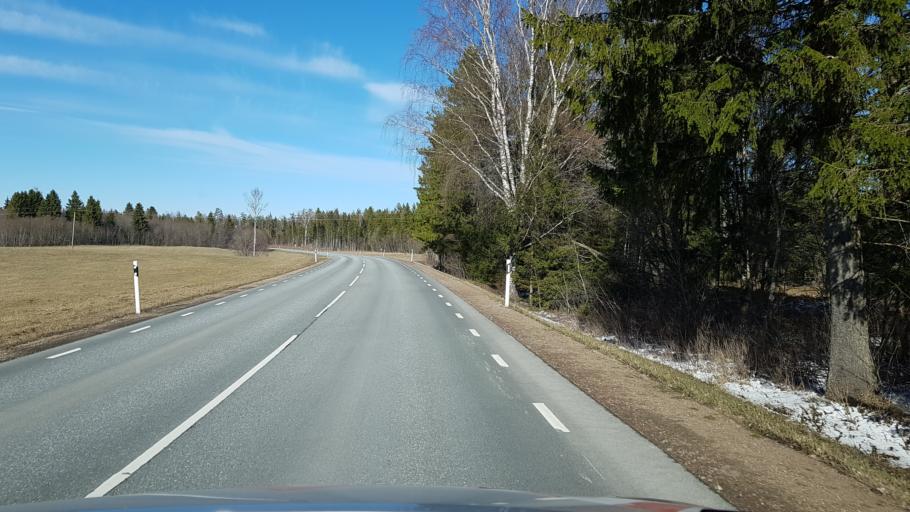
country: EE
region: Laeaene-Virumaa
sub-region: Tapa vald
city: Tapa
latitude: 59.3821
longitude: 26.0136
